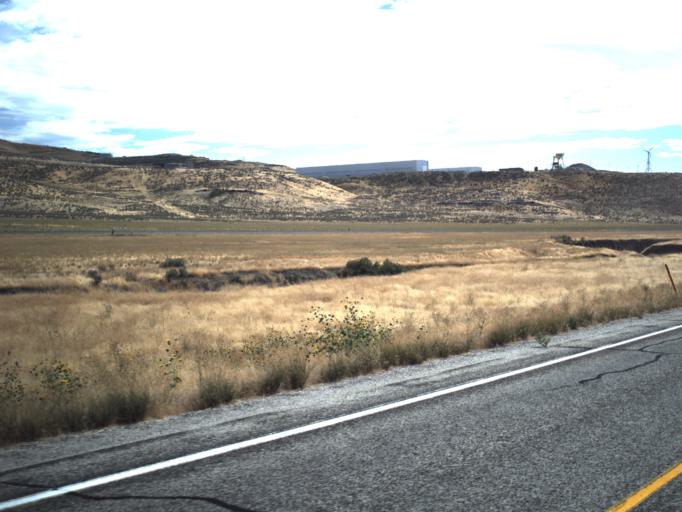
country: US
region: Utah
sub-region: Box Elder County
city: Tremonton
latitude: 41.6823
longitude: -112.4444
